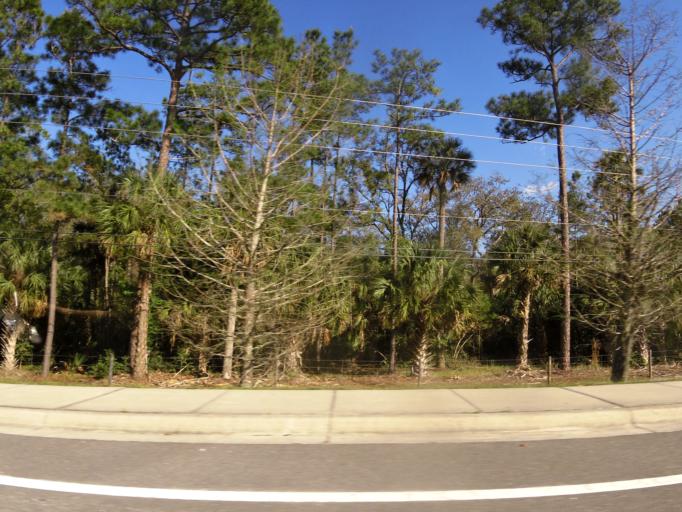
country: US
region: Florida
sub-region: Saint Johns County
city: Palm Valley
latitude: 30.1358
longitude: -81.3810
